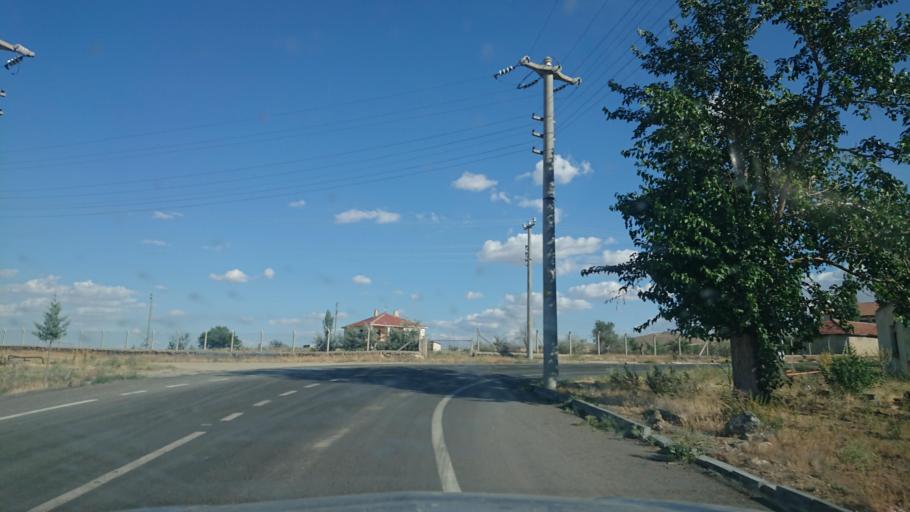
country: TR
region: Aksaray
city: Sariyahsi
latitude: 38.9861
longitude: 33.8531
